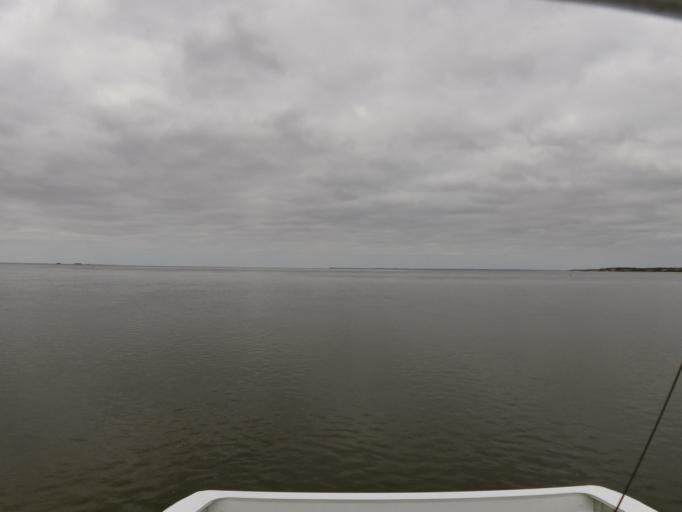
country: DE
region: Schleswig-Holstein
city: Langeness
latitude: 54.6761
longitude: 8.6028
